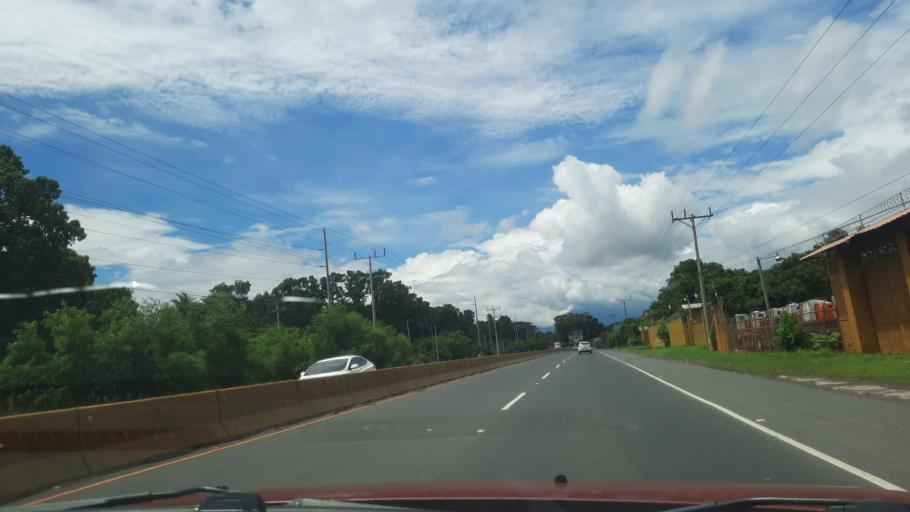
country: SV
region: Sonsonate
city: Acajutla
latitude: 13.6436
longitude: -89.7730
